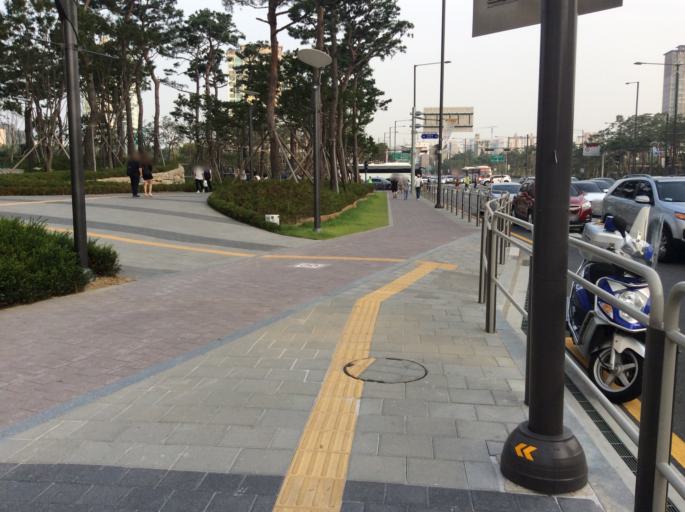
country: KR
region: Gyeonggi-do
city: Seongnam-si
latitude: 37.5121
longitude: 127.1016
